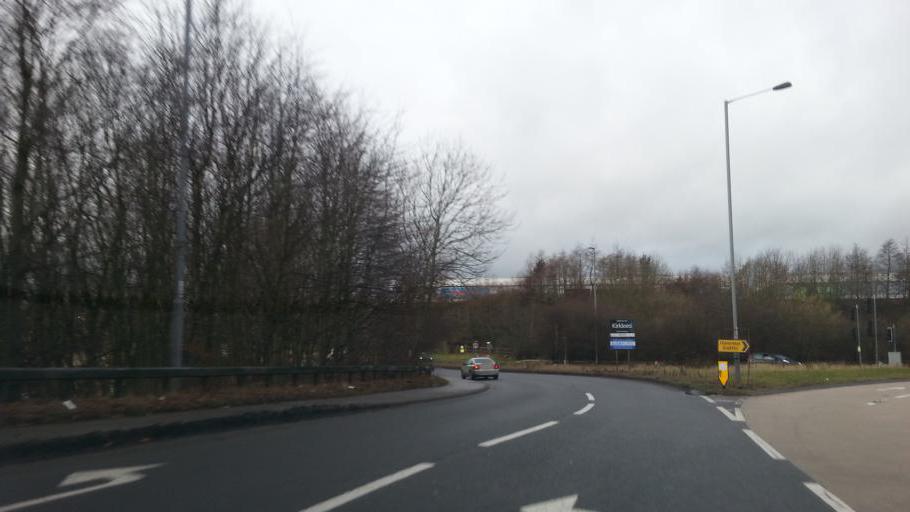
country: GB
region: England
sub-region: City and Borough of Leeds
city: Gildersome
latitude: 53.7456
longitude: -1.6397
